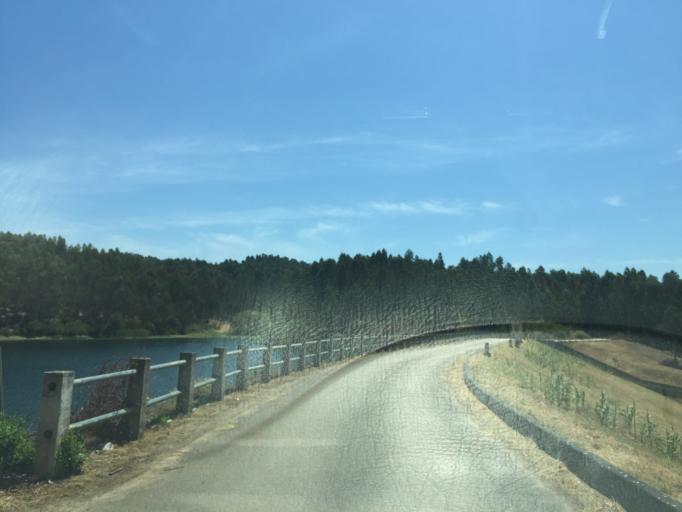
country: PT
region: Santarem
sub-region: Tomar
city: Tomar
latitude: 39.6094
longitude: -8.3593
